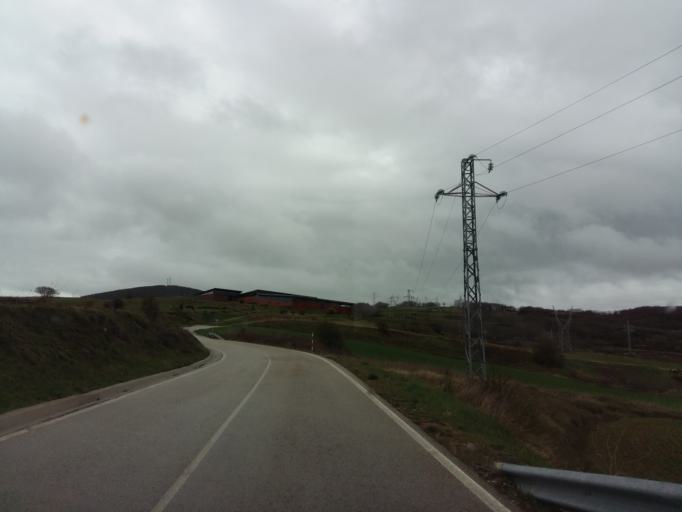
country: ES
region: Cantabria
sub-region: Provincia de Cantabria
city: Mataporquera
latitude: 42.8853
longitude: -4.1588
